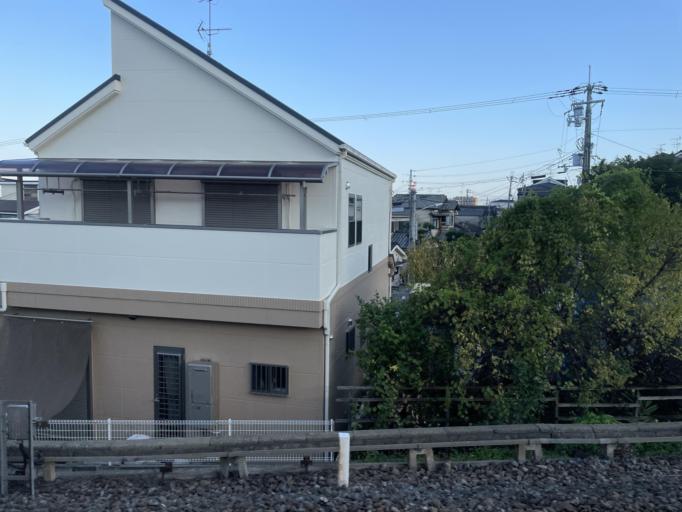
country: JP
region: Osaka
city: Daitocho
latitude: 34.6627
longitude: 135.6441
